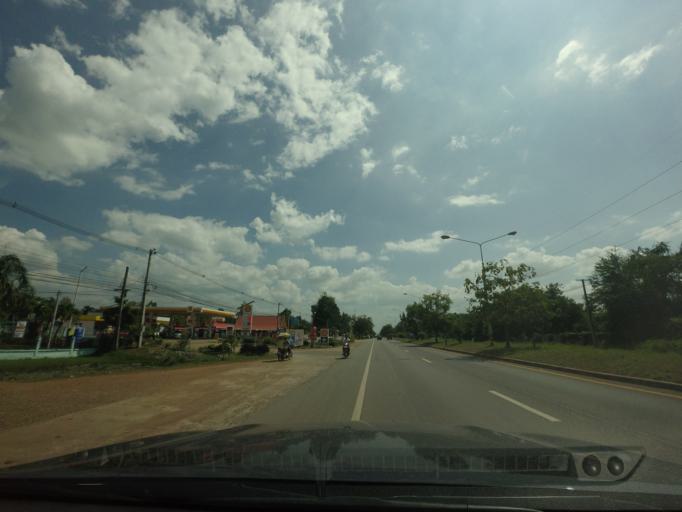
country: TH
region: Phetchabun
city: Nong Phai
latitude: 15.9117
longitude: 101.0268
